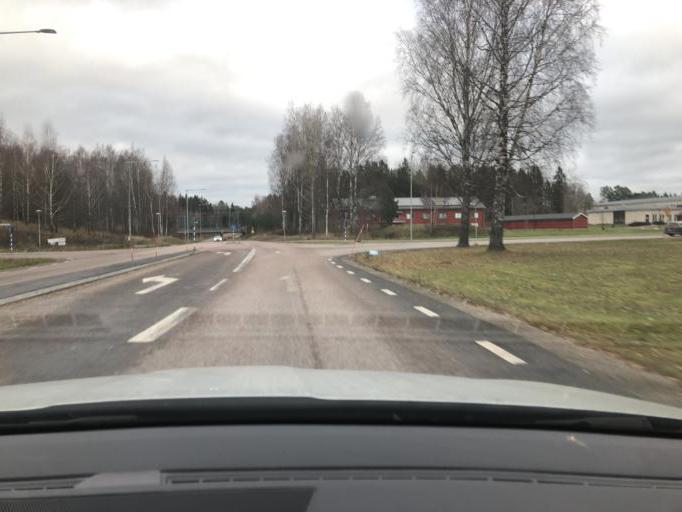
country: SE
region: Uppsala
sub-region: Tierps Kommun
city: Tierp
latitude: 60.3483
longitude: 17.4968
